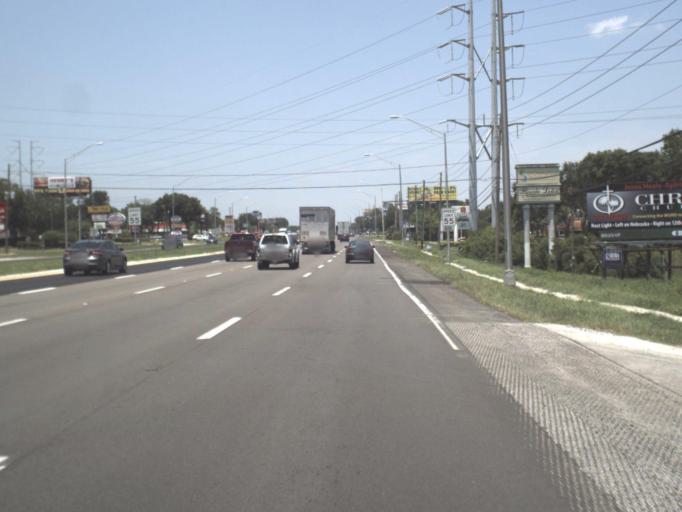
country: US
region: Florida
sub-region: Pinellas County
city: Saint George
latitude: 28.0692
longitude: -82.7387
